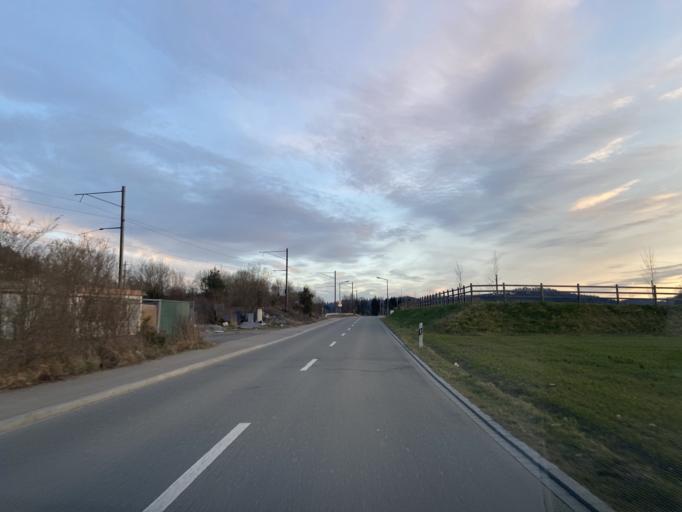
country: CH
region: Zurich
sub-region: Bezirk Winterthur
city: Wuelflingen (Kreis 6) / Lindenplatz
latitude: 47.5207
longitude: 8.6954
